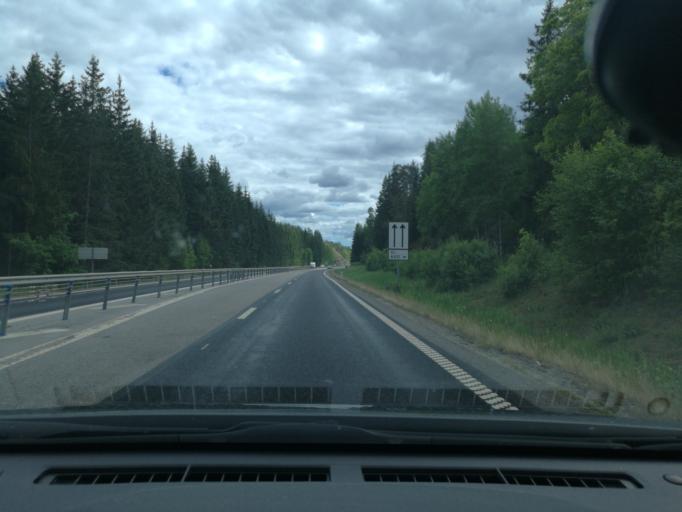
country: SE
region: OEstergoetland
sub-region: Valdemarsviks Kommun
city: Valdemarsvik
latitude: 58.1846
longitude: 16.5361
